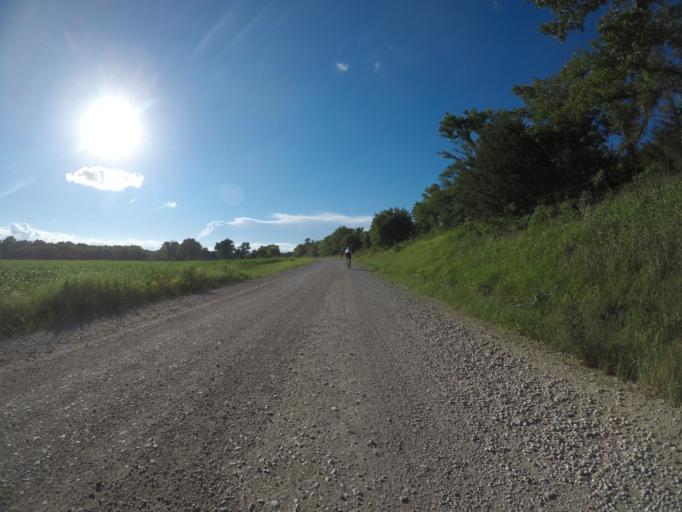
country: US
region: Kansas
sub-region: Riley County
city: Ogden
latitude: 39.2430
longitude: -96.7321
